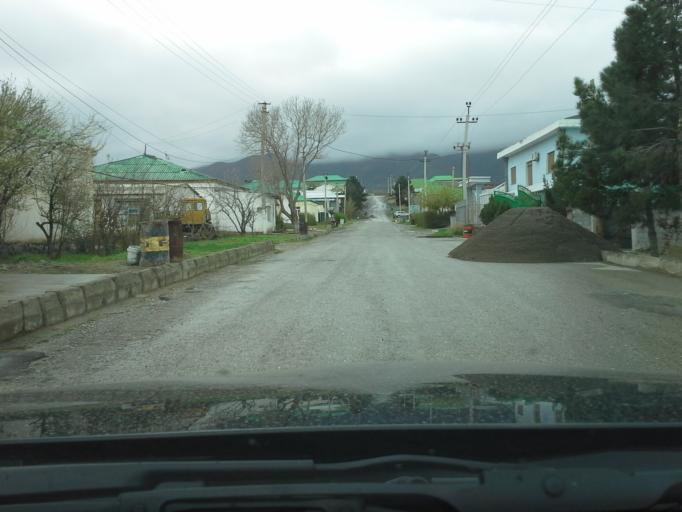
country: TM
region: Ahal
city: Abadan
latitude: 37.9635
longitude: 58.2050
